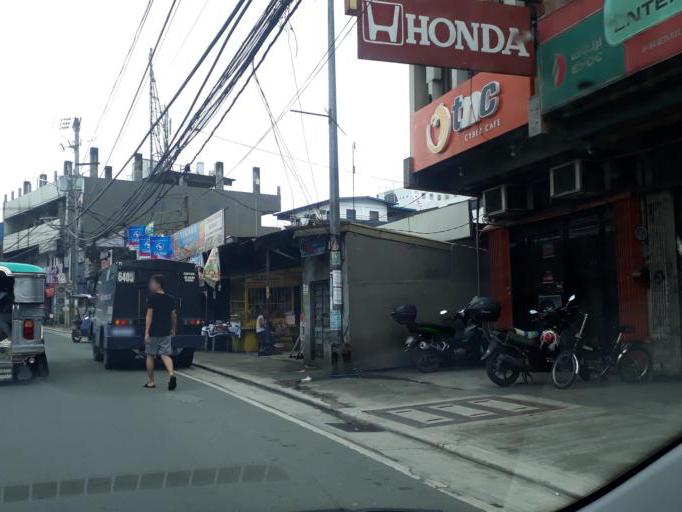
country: PH
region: Calabarzon
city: Del Monte
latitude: 14.6347
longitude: 121.0179
